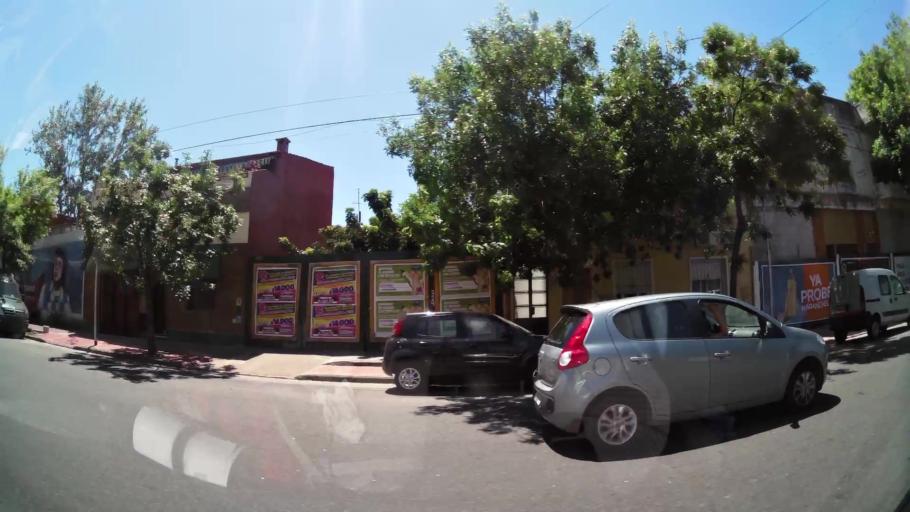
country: AR
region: Buenos Aires F.D.
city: Buenos Aires
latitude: -34.6398
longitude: -58.3973
